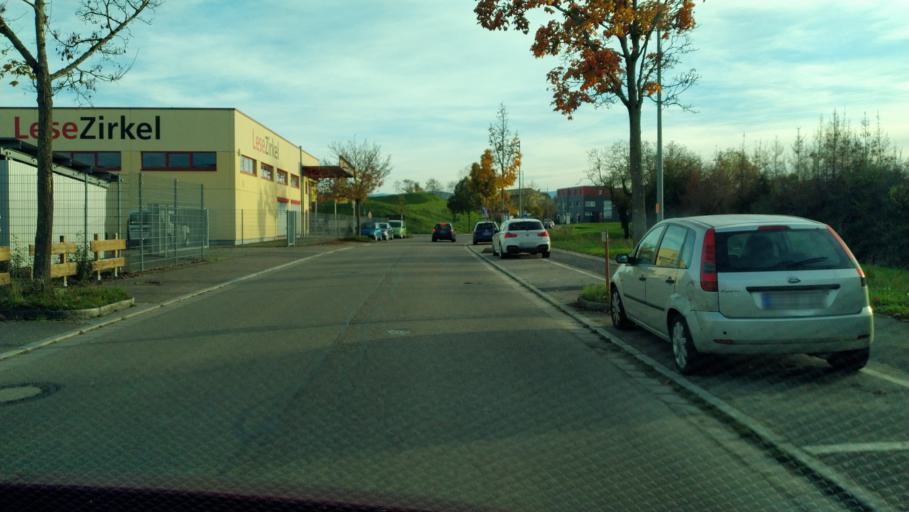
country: DE
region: Baden-Wuerttemberg
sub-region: Freiburg Region
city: Emmendingen
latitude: 48.1108
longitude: 7.8481
